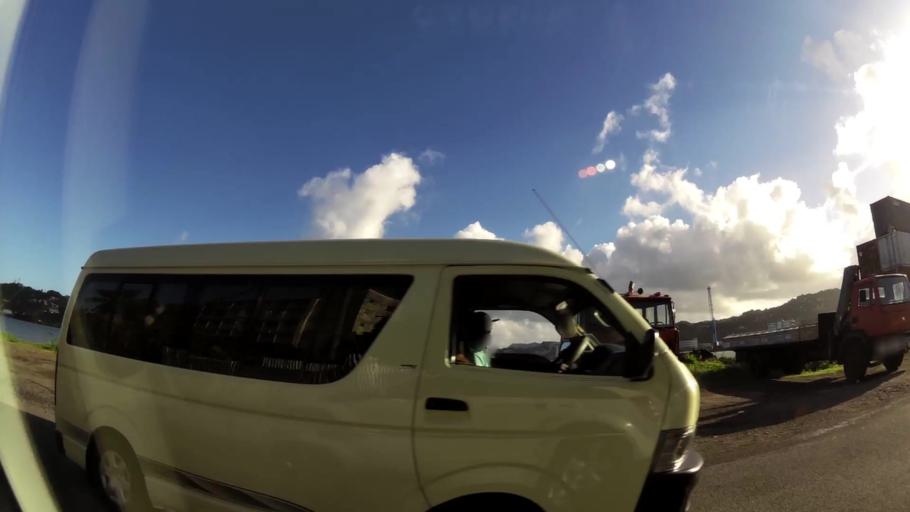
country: LC
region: Castries Quarter
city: Castries
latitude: 14.0103
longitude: -60.9978
